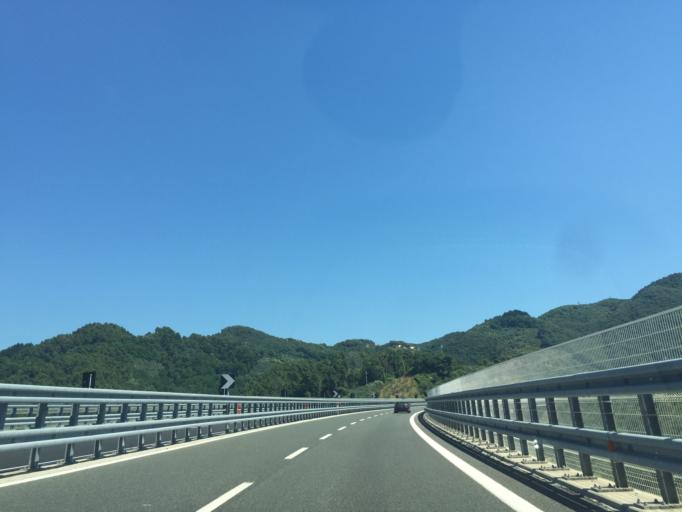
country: IT
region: Tuscany
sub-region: Provincia di Lucca
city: Massarosa
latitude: 43.8707
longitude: 10.3598
